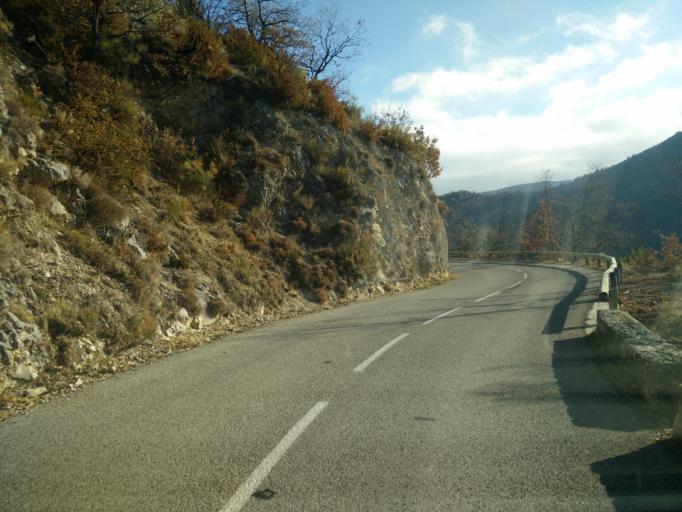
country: FR
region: Provence-Alpes-Cote d'Azur
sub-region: Departement des Alpes-Maritimes
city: Le Broc
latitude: 43.8122
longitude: 7.0978
